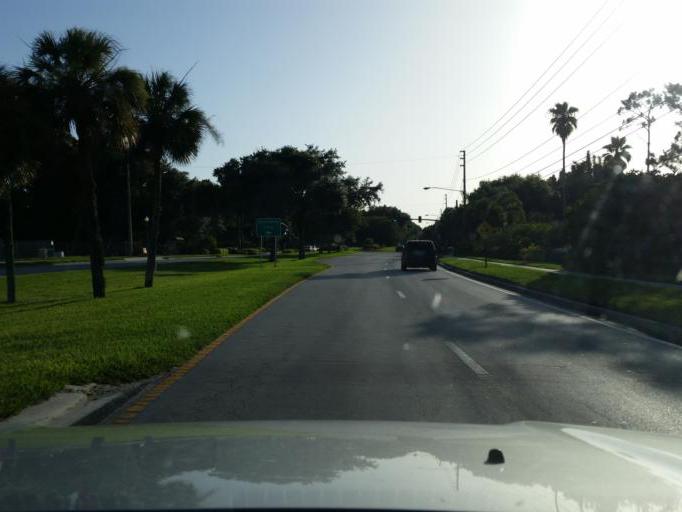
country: US
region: Florida
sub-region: Orange County
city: Williamsburg
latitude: 28.4065
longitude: -81.4583
